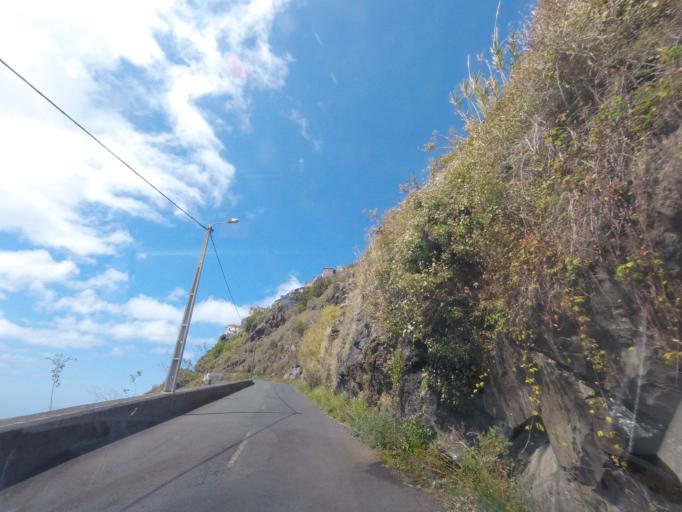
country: PT
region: Madeira
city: Ponta do Sol
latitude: 32.6807
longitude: -17.0795
